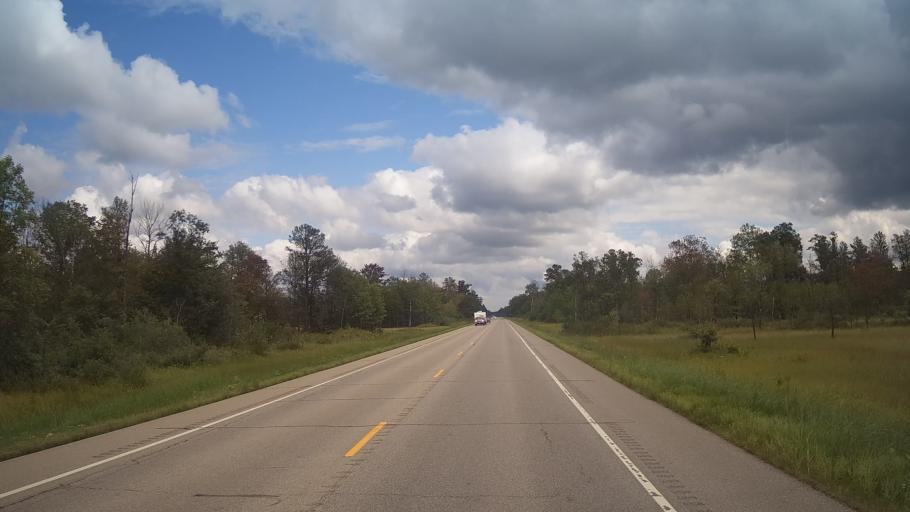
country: US
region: Wisconsin
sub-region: Adams County
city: Friendship
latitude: 44.0253
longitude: -89.7244
